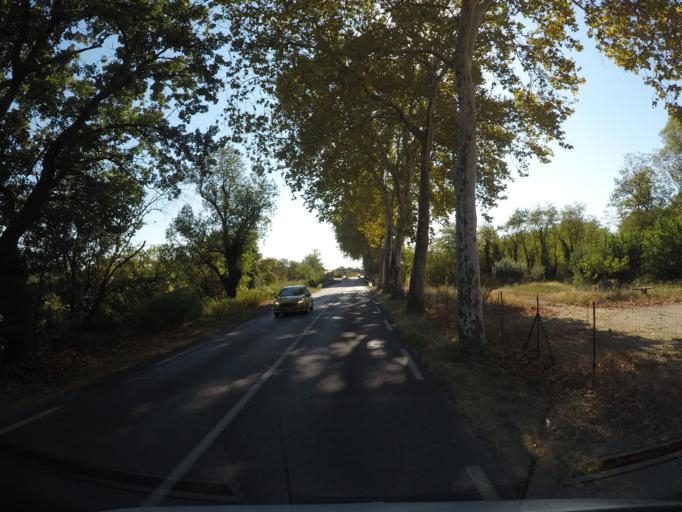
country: FR
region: Languedoc-Roussillon
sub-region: Departement du Gard
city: Boisset-et-Gaujac
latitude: 44.0301
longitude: 4.0143
